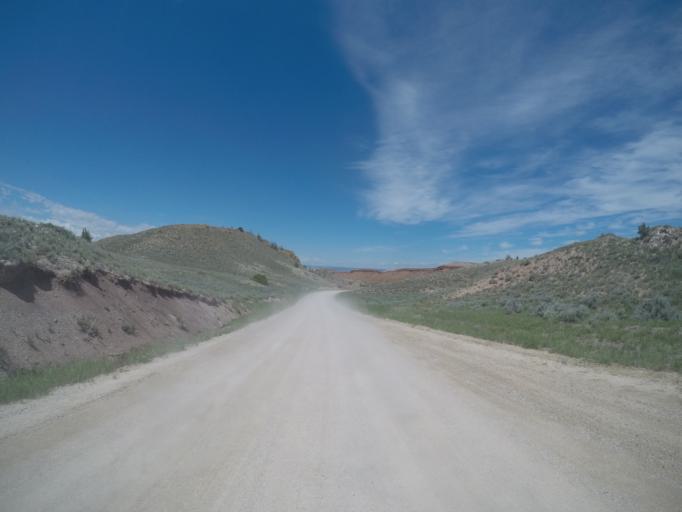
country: US
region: Montana
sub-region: Carbon County
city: Red Lodge
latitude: 45.2083
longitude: -108.8030
